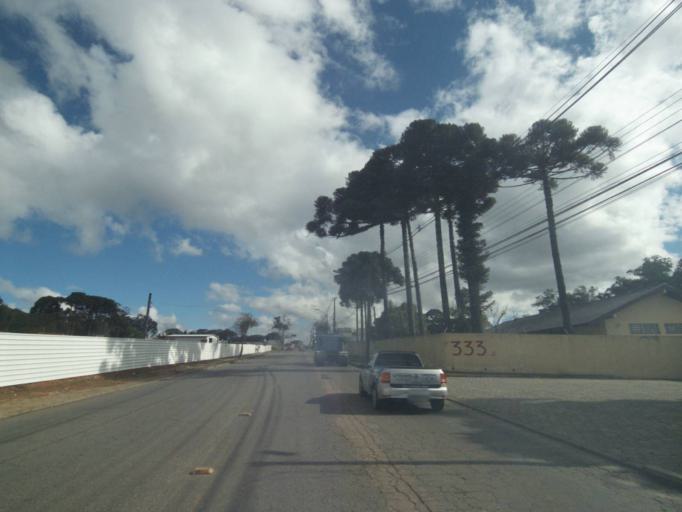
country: BR
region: Parana
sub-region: Sao Jose Dos Pinhais
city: Sao Jose dos Pinhais
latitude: -25.5305
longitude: -49.2952
